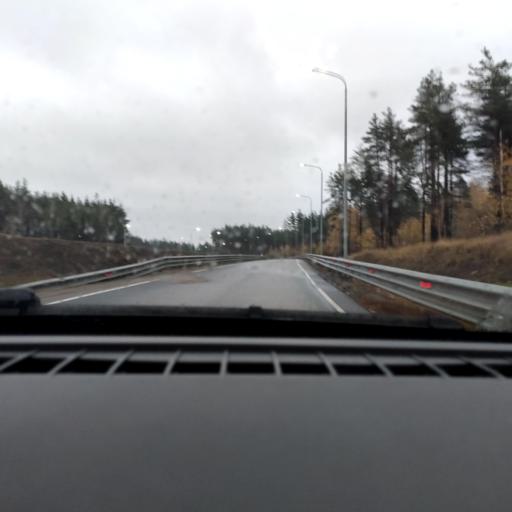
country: RU
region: Voronezj
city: Somovo
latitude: 51.6900
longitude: 39.3036
